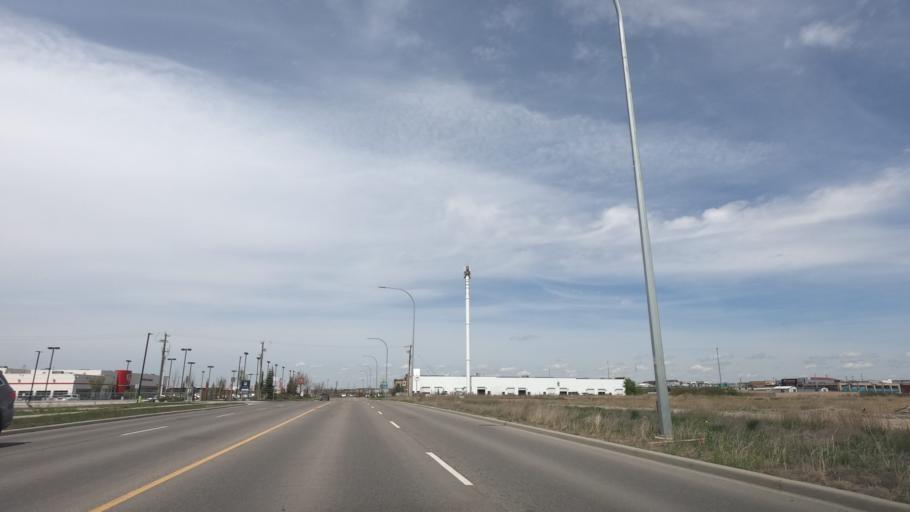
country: CA
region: Alberta
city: Airdrie
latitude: 51.2567
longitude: -114.0051
